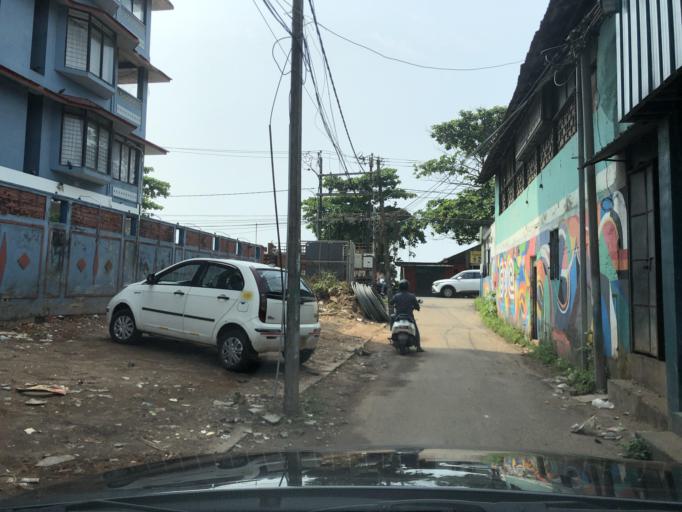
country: IN
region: Kerala
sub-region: Kozhikode
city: Kozhikode
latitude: 11.2471
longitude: 75.7733
